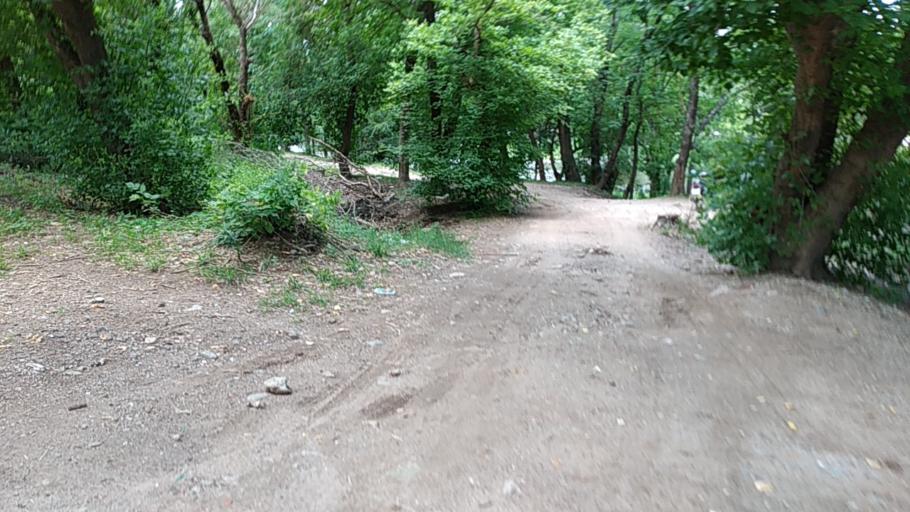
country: AR
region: Cordoba
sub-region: Departamento de Calamuchita
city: Santa Rosa de Calamuchita
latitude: -32.0602
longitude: -64.5564
